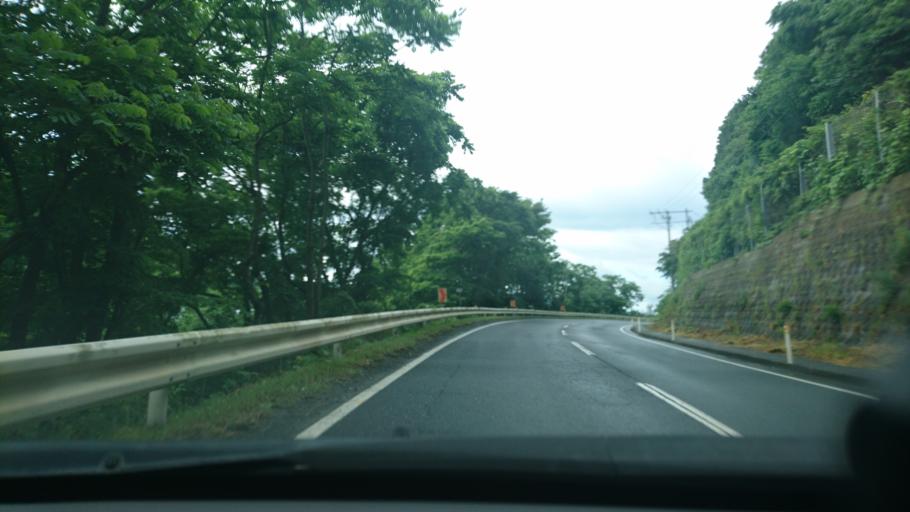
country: JP
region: Miyagi
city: Wakuya
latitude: 38.5955
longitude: 141.3043
